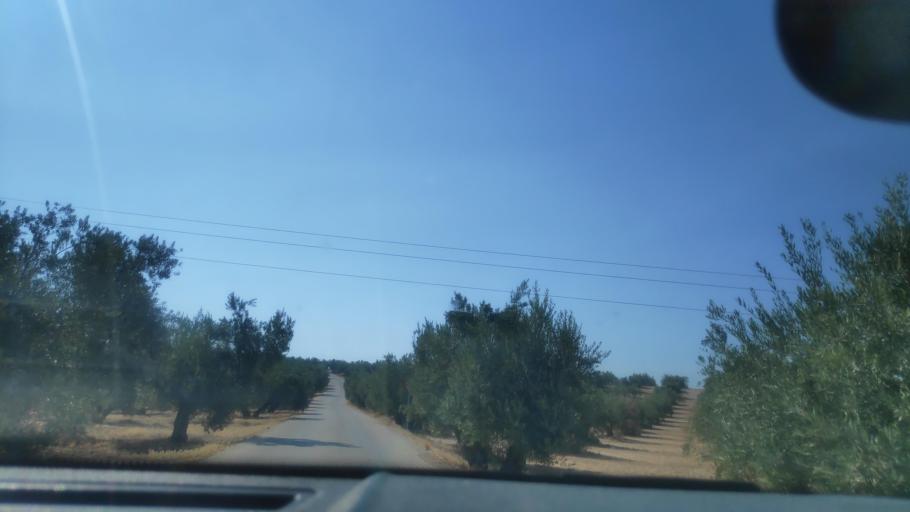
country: ES
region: Andalusia
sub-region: Provincia de Jaen
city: Jaen
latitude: 37.8286
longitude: -3.7594
